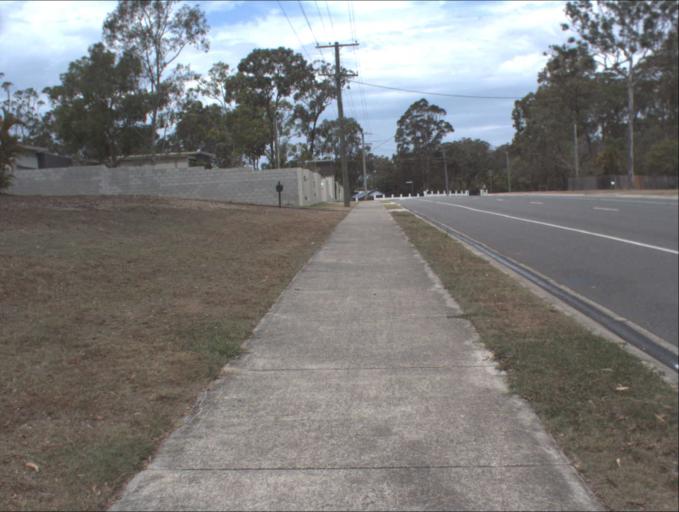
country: AU
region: Queensland
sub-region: Logan
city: Beenleigh
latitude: -27.6672
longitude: 153.2204
